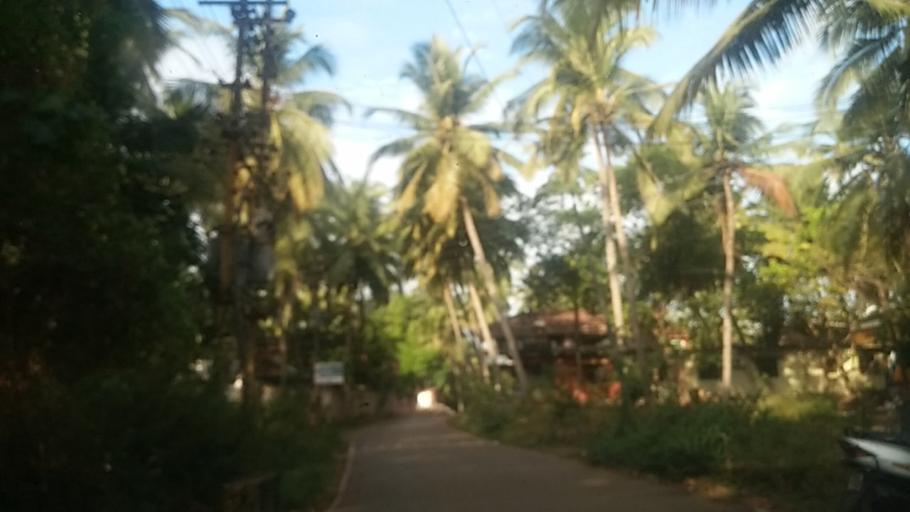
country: IN
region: Goa
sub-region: South Goa
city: Cuncolim
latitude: 15.1809
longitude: 73.9694
